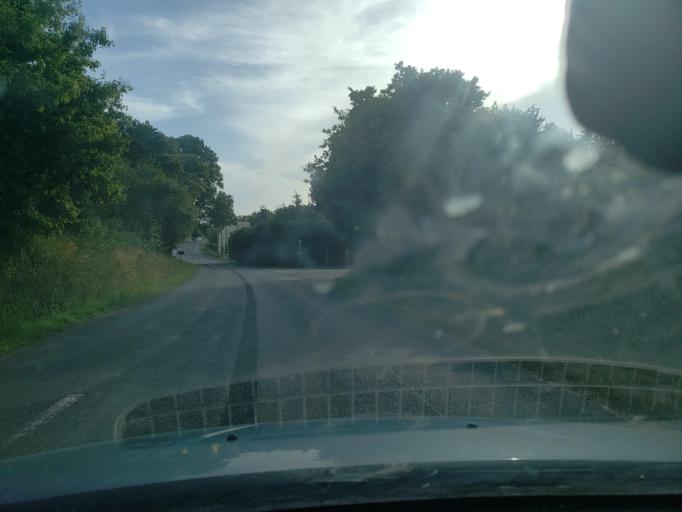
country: FR
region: Brittany
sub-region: Departement du Finistere
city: Plobannalec-Lesconil
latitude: 47.8171
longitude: -4.2327
